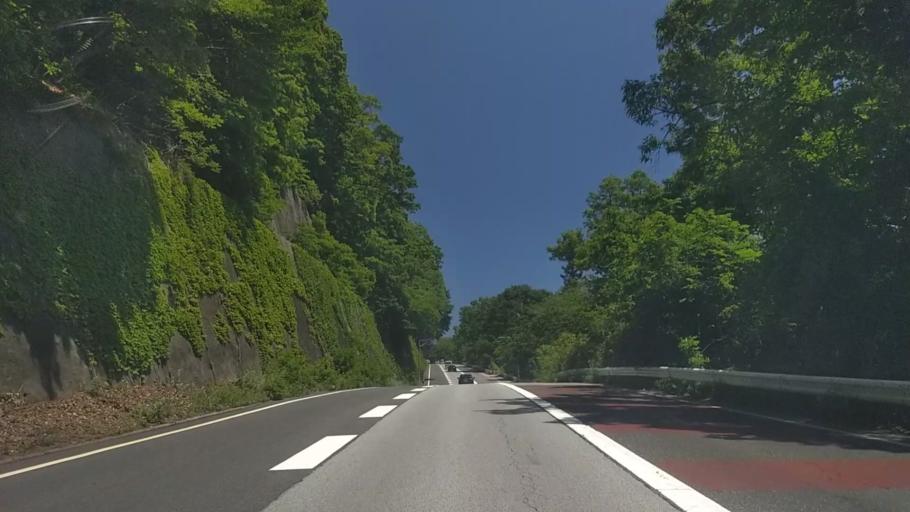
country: JP
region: Yamanashi
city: Nirasaki
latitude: 35.8029
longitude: 138.4263
